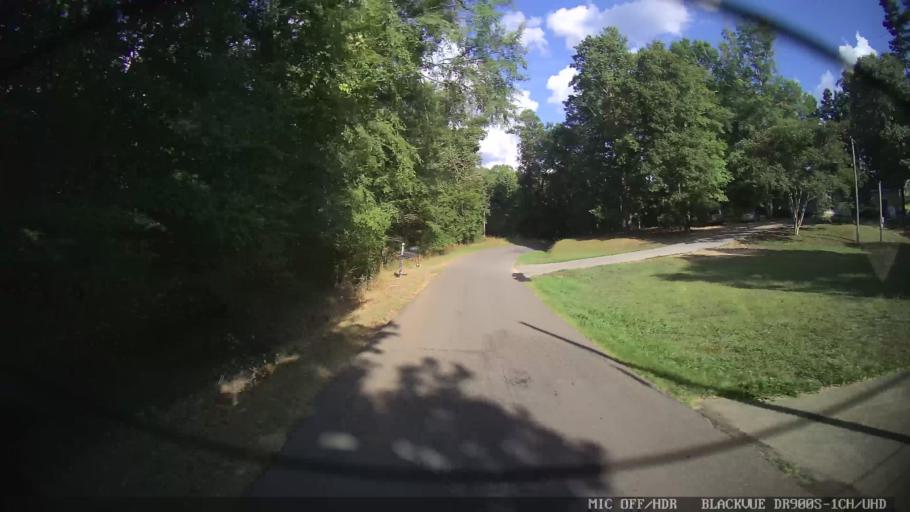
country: US
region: Georgia
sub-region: Floyd County
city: Lindale
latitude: 34.2143
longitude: -85.1270
